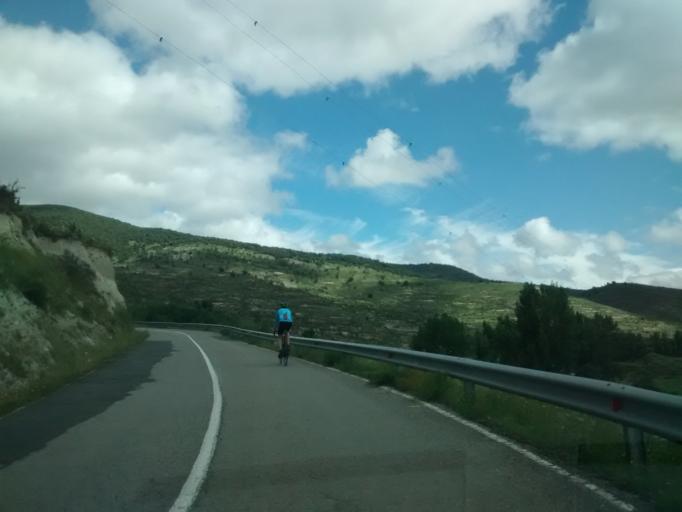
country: ES
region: La Rioja
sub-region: Provincia de La Rioja
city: Terroba
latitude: 42.2495
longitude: -2.4537
